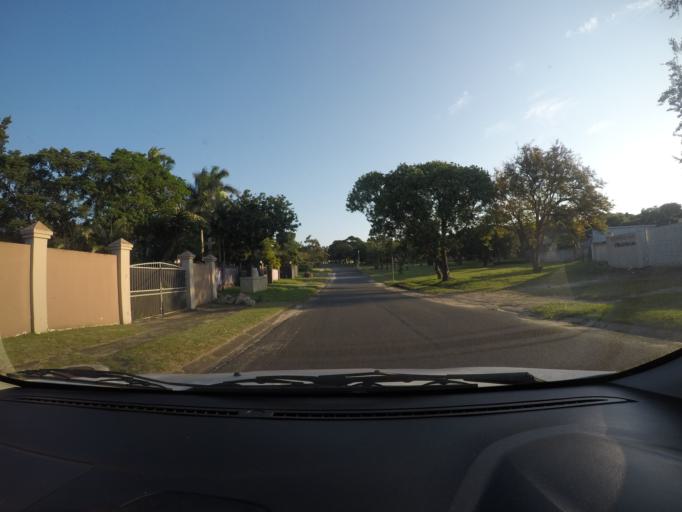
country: ZA
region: KwaZulu-Natal
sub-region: uThungulu District Municipality
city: Richards Bay
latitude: -28.7832
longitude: 32.0932
